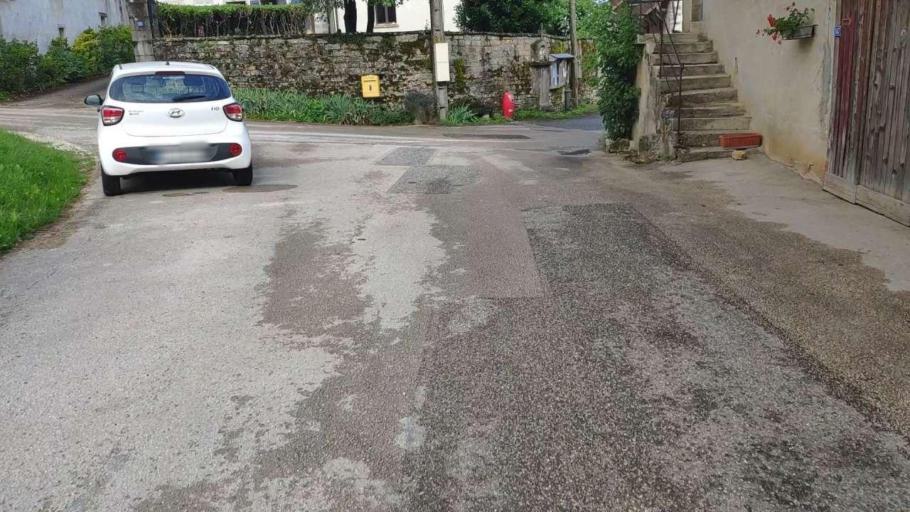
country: FR
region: Franche-Comte
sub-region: Departement du Jura
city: Poligny
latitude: 46.8025
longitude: 5.5886
